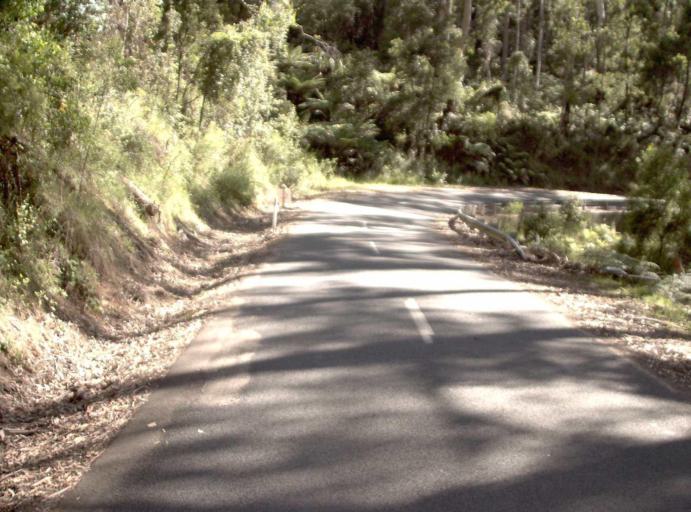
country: AU
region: New South Wales
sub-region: Bombala
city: Bombala
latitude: -37.3799
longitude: 148.6261
